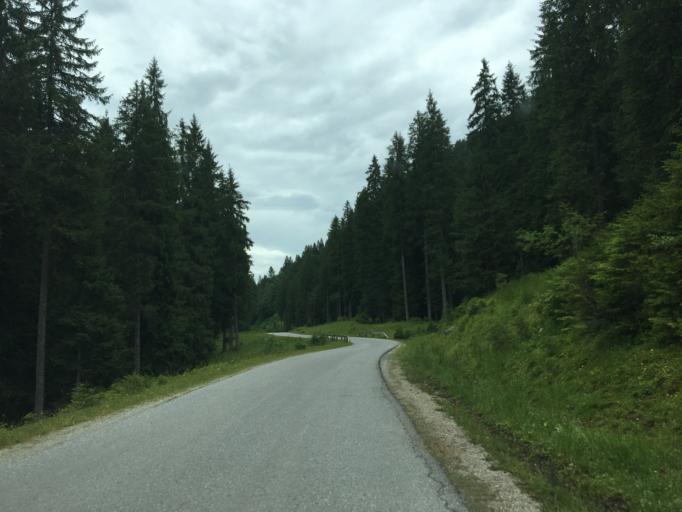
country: AT
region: Salzburg
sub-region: Politischer Bezirk Hallein
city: Abtenau
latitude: 47.6369
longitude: 13.4177
